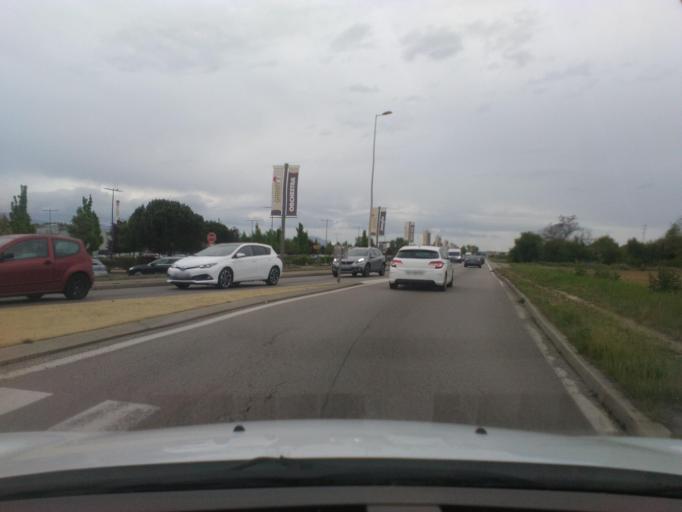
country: FR
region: Rhone-Alpes
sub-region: Departement de l'Isere
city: Chanas
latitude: 45.3279
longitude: 4.8067
